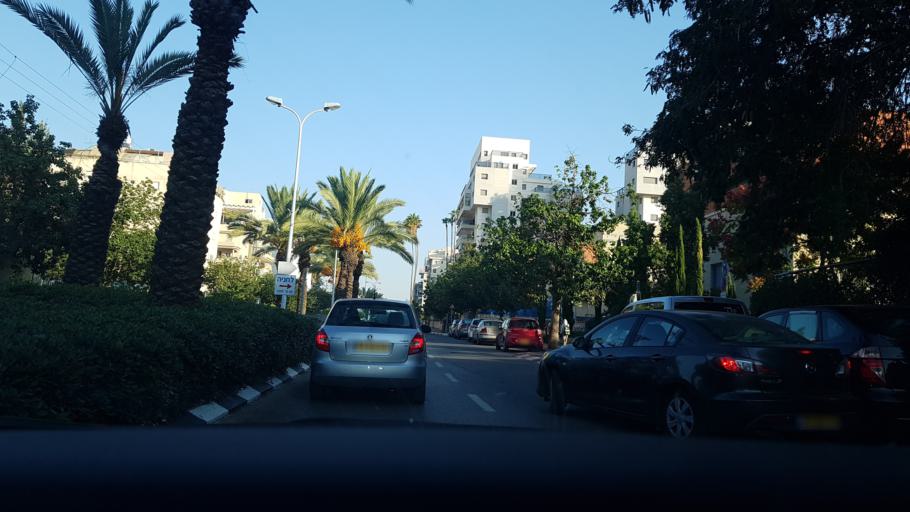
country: IL
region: Central District
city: Ness Ziona
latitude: 31.8999
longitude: 34.8199
